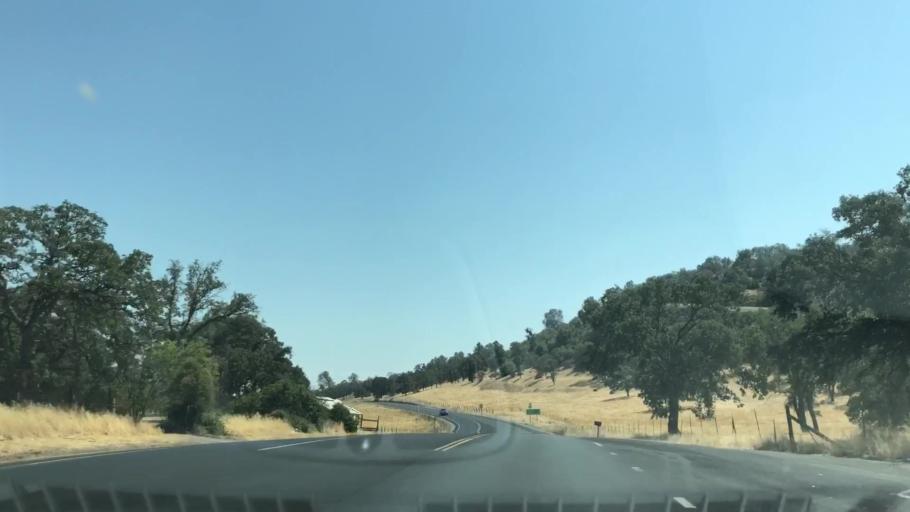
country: US
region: California
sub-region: Tuolumne County
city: Jamestown
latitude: 37.8879
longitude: -120.4862
